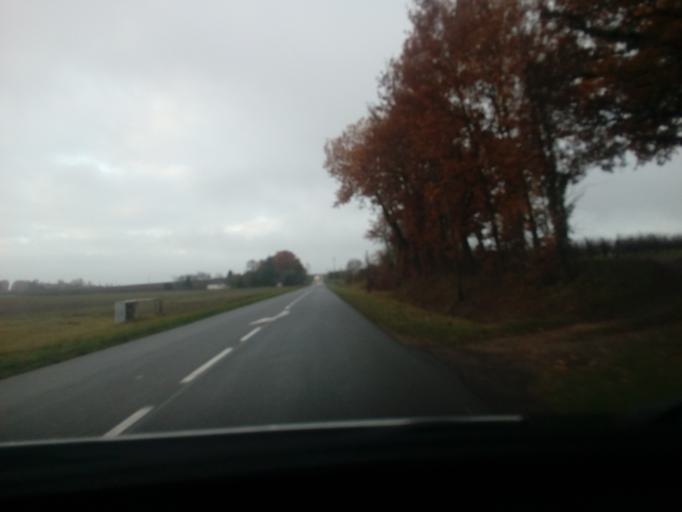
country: FR
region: Poitou-Charentes
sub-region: Departement de la Charente
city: Baignes-Sainte-Radegonde
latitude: 45.4554
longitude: -0.2498
